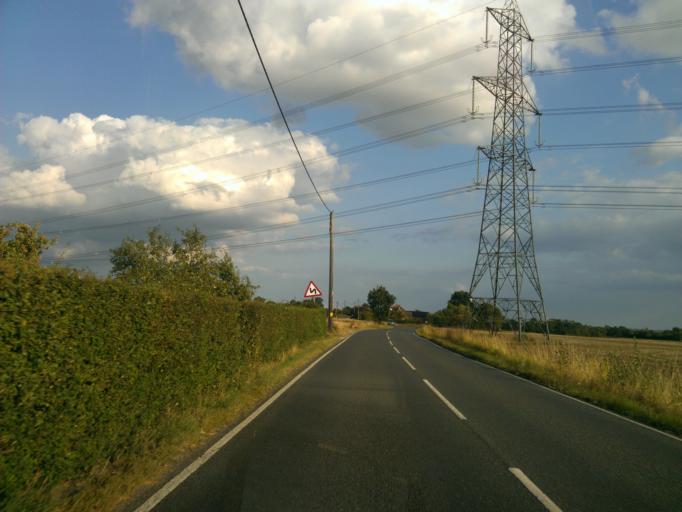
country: GB
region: England
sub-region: Essex
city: Rayne
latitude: 51.8636
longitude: 0.5917
